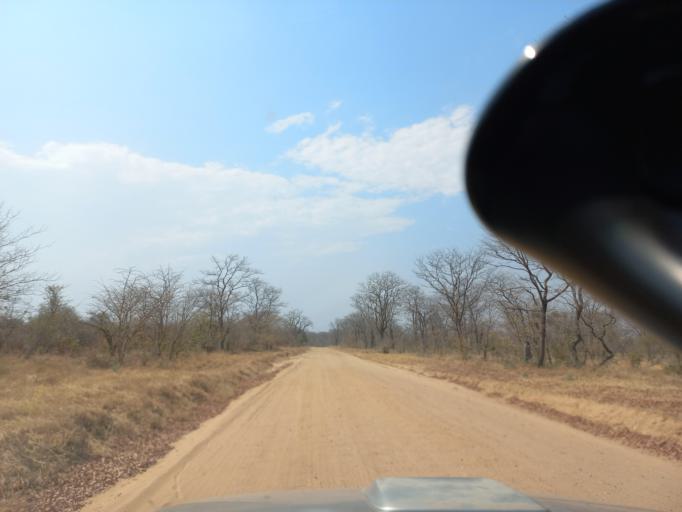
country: ZW
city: Chirundu
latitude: -15.9348
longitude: 28.9149
